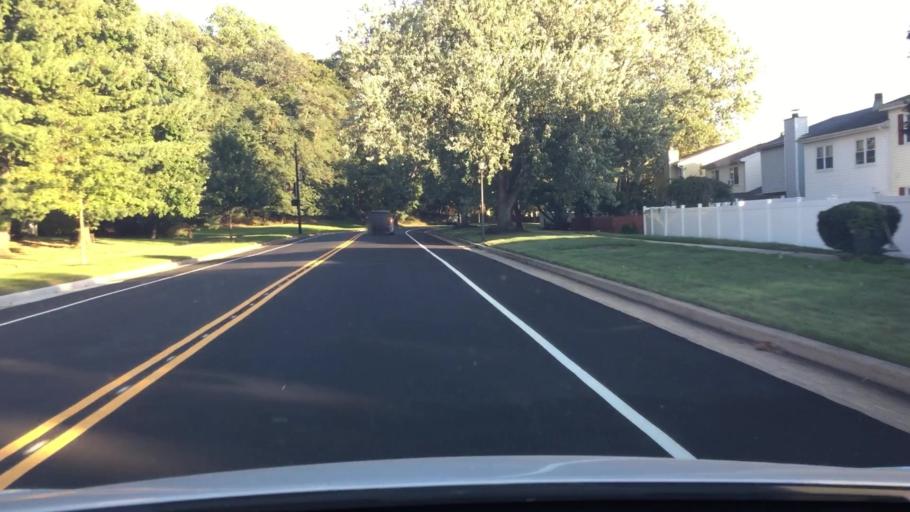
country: US
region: Pennsylvania
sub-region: Bucks County
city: Newtown
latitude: 40.2204
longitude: -74.9526
